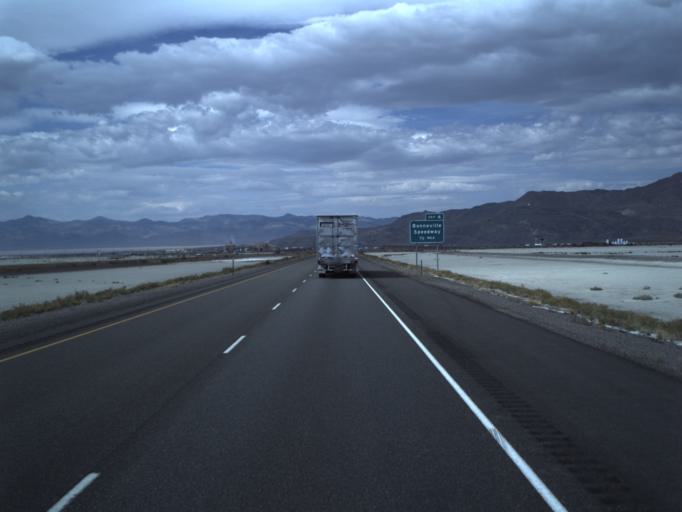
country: US
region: Utah
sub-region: Tooele County
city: Wendover
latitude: 40.7414
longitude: -113.9514
